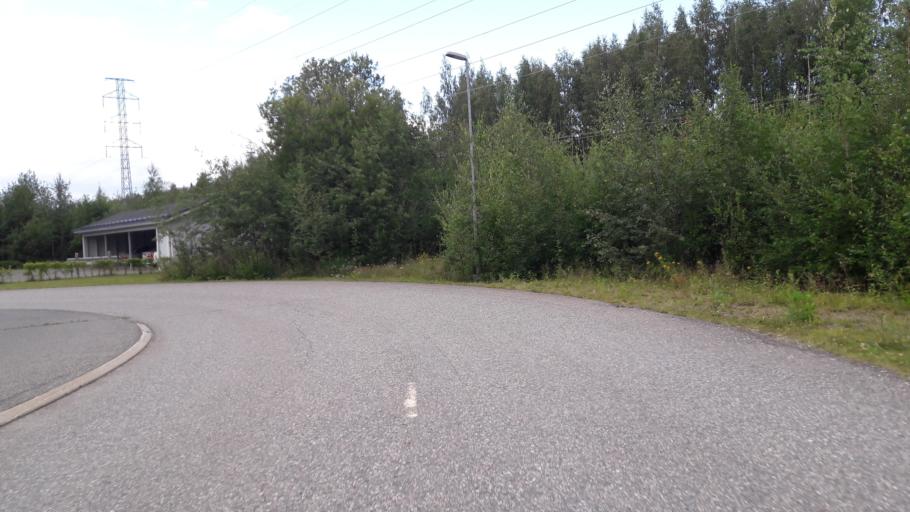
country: FI
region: North Karelia
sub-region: Joensuu
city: Joensuu
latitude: 62.5919
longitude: 29.8040
